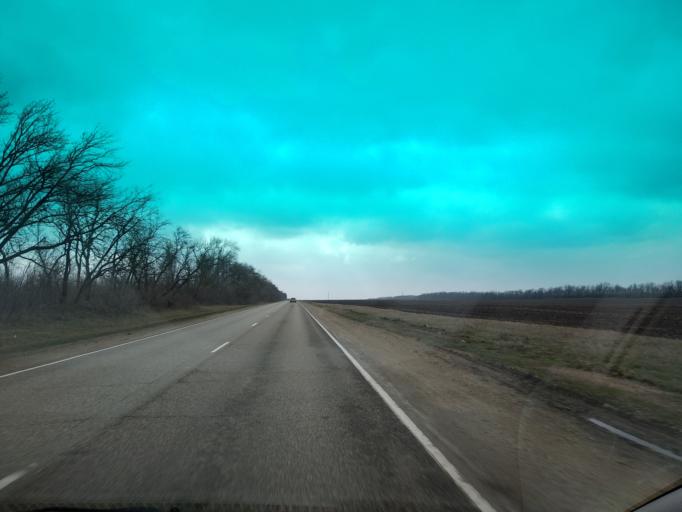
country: RU
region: Krasnodarskiy
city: Novorozhdestvenskaya
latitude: 45.7494
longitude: 39.9199
